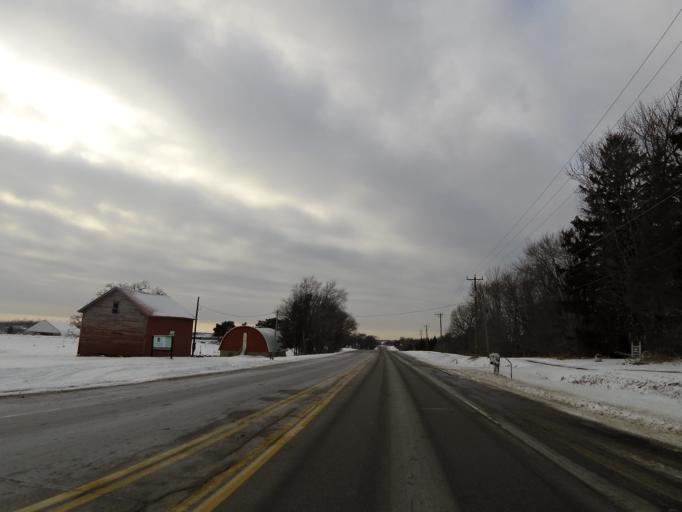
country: US
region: Minnesota
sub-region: Washington County
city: Woodbury
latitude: 44.8910
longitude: -92.8864
